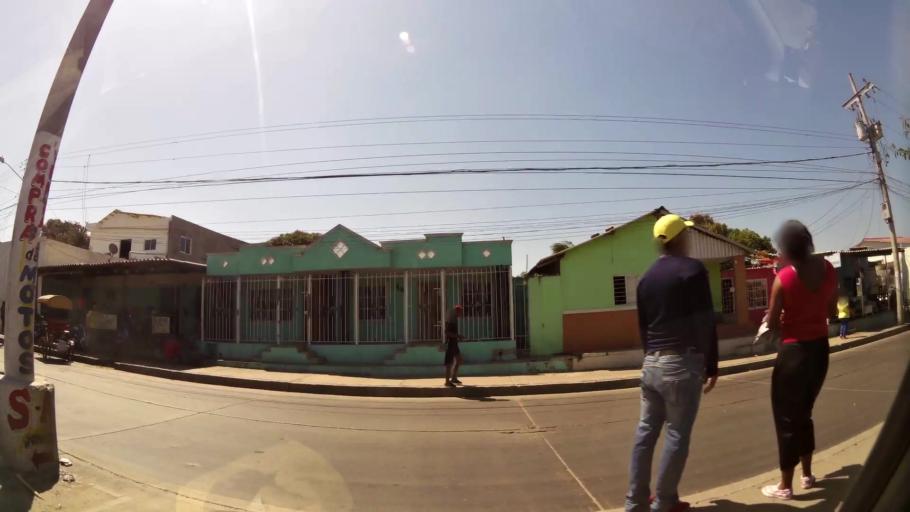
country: CO
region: Atlantico
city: Barranquilla
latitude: 10.9614
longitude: -74.7750
